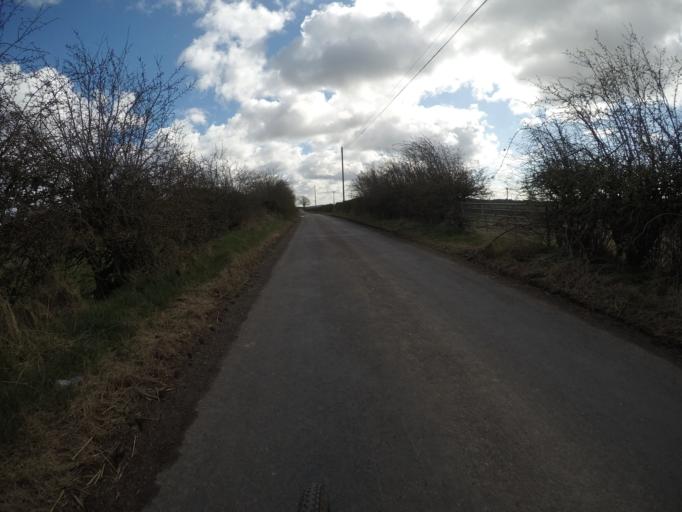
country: GB
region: Scotland
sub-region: North Ayrshire
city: Dreghorn
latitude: 55.5900
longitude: -4.5937
